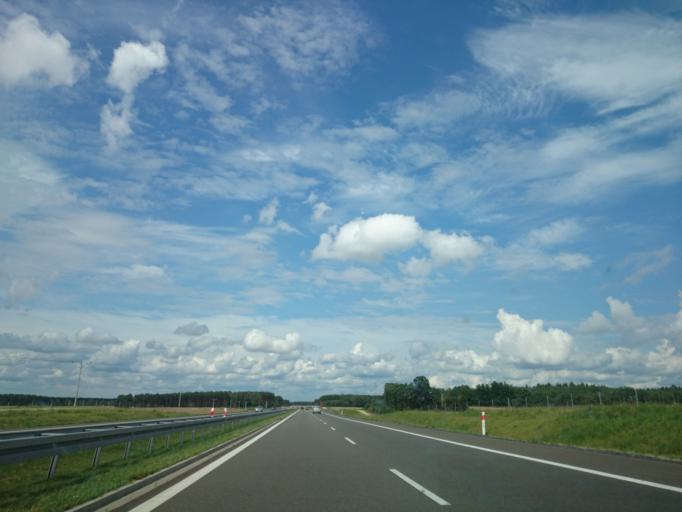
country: PL
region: Lubusz
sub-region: Powiat zielonogorski
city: Sulechow
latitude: 52.1663
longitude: 15.5877
